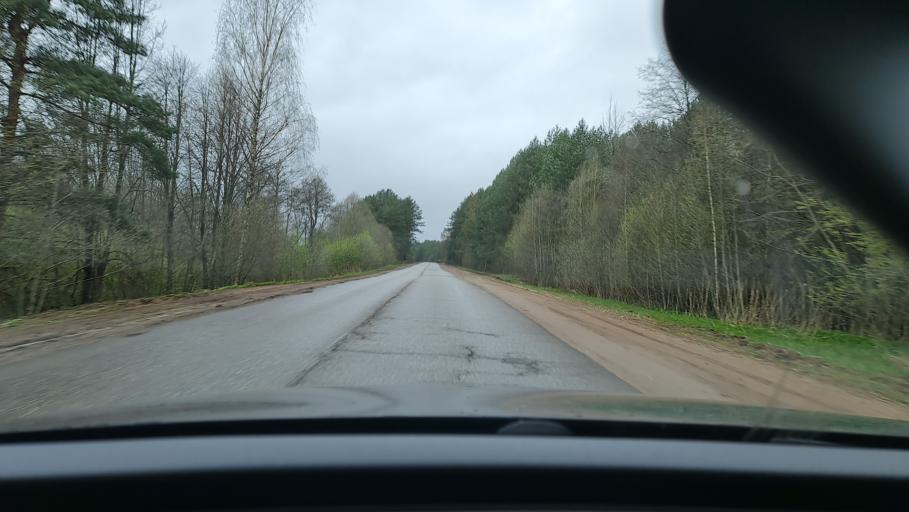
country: RU
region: Novgorod
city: Demyansk
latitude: 57.6580
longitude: 32.4958
